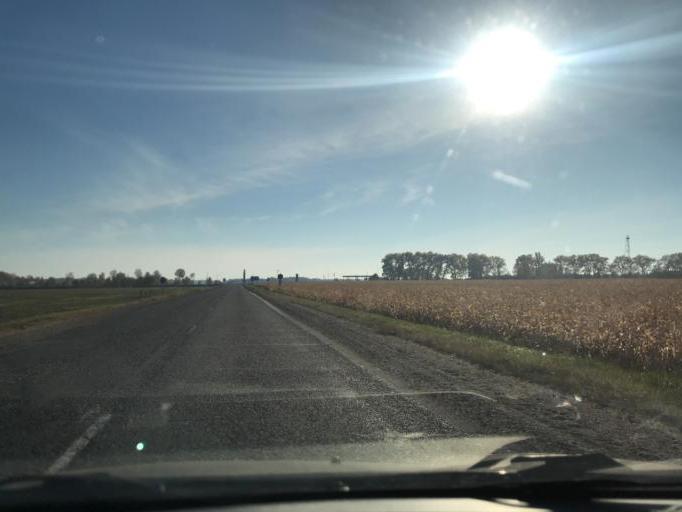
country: BY
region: Gomel
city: Brahin
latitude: 51.7779
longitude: 30.2420
